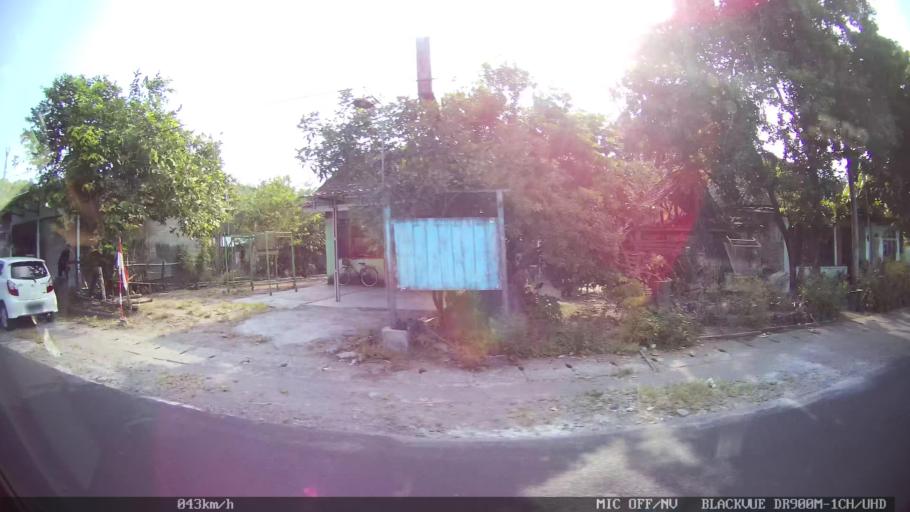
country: ID
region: Daerah Istimewa Yogyakarta
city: Bantul
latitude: -7.8669
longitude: 110.3184
